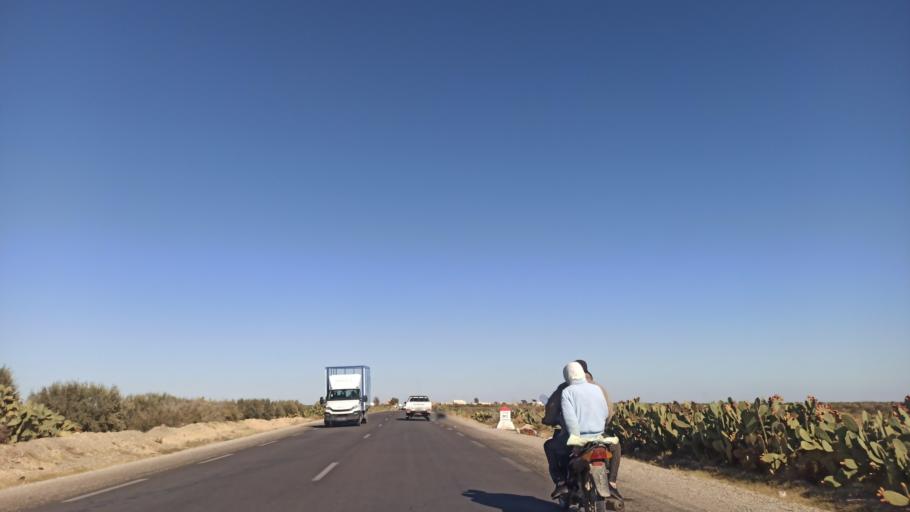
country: TN
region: Sidi Bu Zayd
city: Bi'r al Hufayy
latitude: 34.9643
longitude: 9.2240
